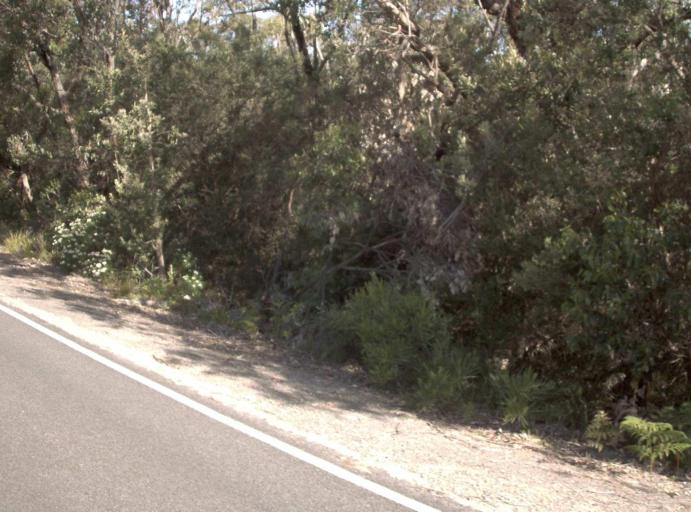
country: AU
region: Victoria
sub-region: East Gippsland
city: Lakes Entrance
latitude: -37.7982
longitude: 148.5909
